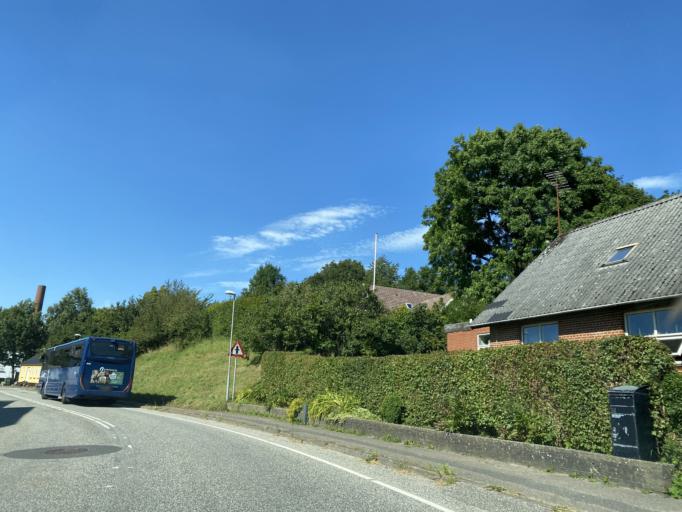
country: DK
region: Central Jutland
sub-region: Hedensted Kommune
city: Torring
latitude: 55.8151
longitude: 9.4609
